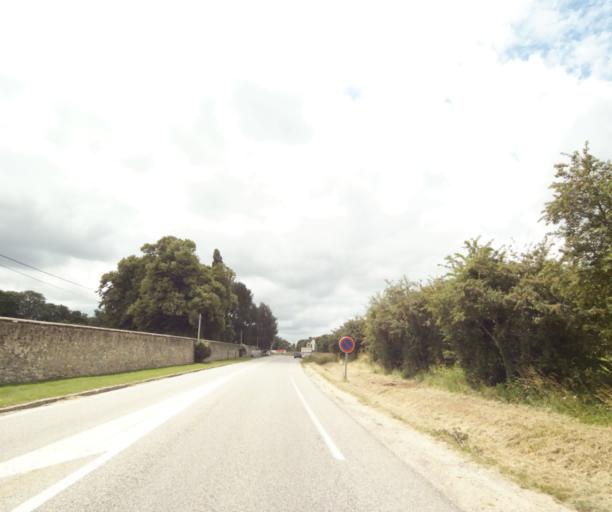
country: FR
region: Ile-de-France
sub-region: Departement des Yvelines
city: Saint-Cyr-l'Ecole
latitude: 48.8172
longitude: 2.0798
